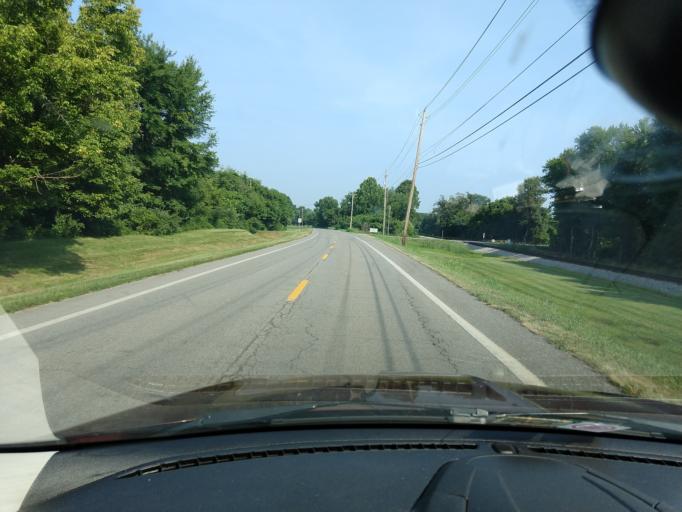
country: US
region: West Virginia
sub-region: Mason County
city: New Haven
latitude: 38.9797
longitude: -81.9446
